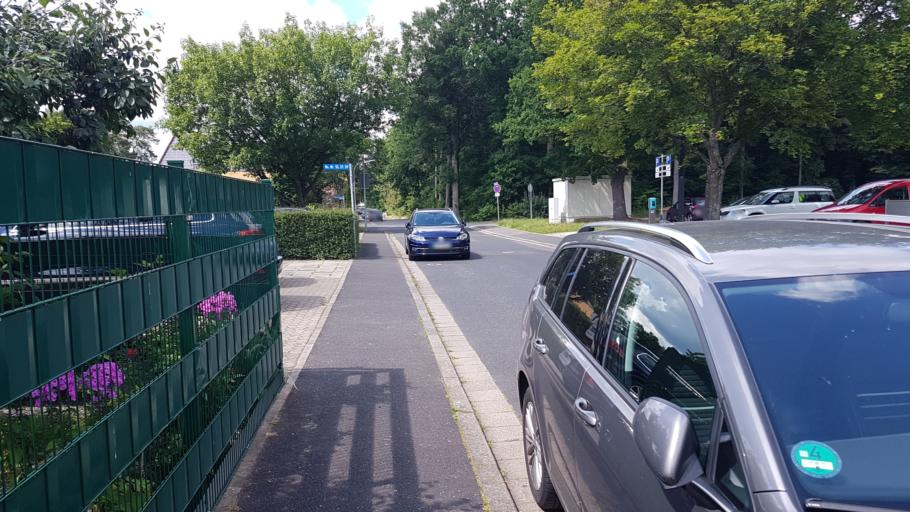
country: DE
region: Bavaria
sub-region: Regierungsbezirk Unterfranken
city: Schwebheim
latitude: 50.0002
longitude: 10.2498
